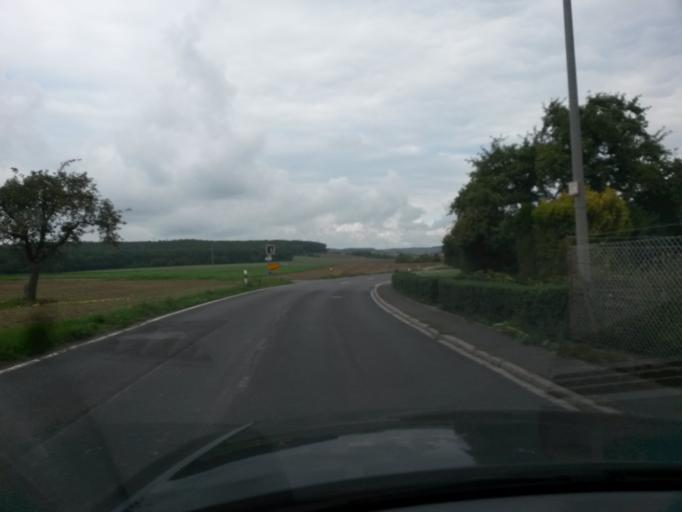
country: DE
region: Bavaria
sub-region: Regierungsbezirk Unterfranken
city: Gadheim
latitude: 49.8466
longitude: 9.9055
